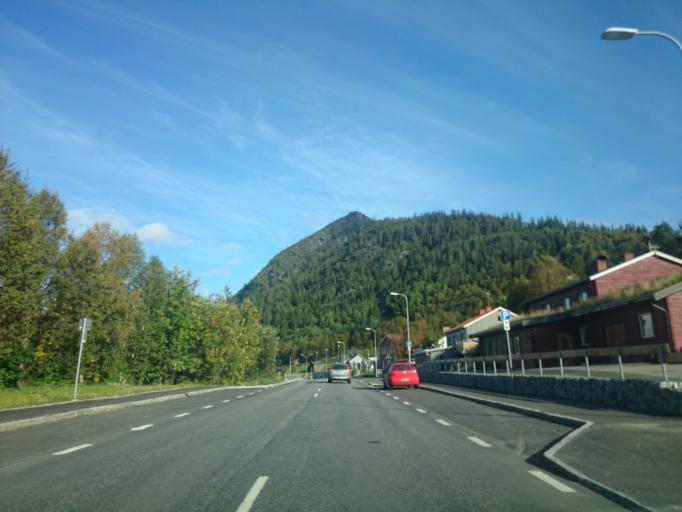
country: NO
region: Hedmark
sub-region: Engerdal
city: Engerdal
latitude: 62.5436
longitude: 12.5470
